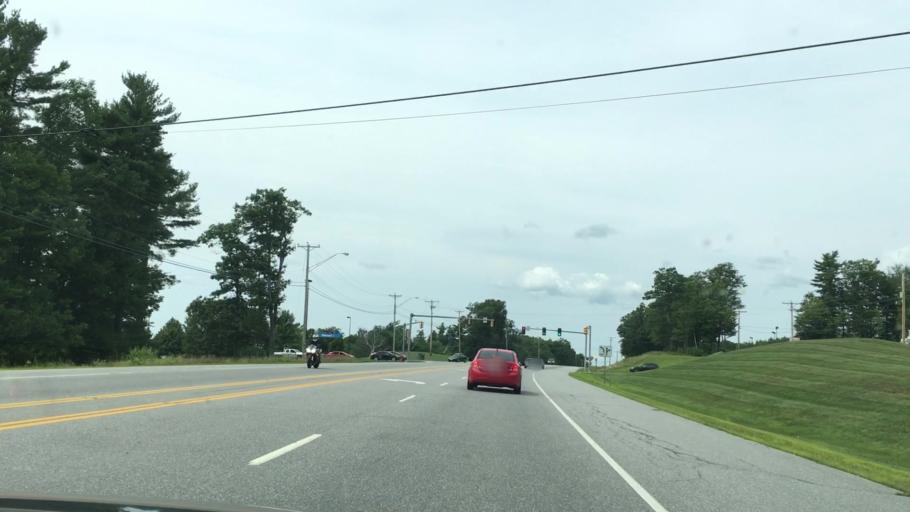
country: US
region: New Hampshire
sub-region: Cheshire County
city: Rindge
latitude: 42.7406
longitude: -72.0368
